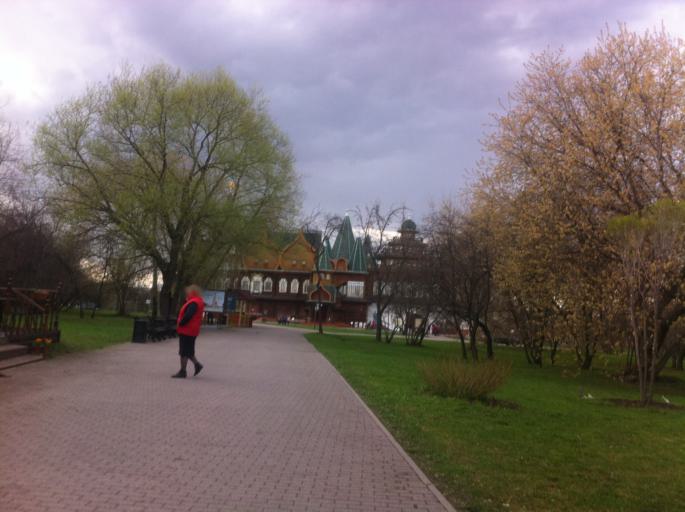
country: RU
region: Moscow
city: Kolomenskoye
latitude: 55.6547
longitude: 37.6592
